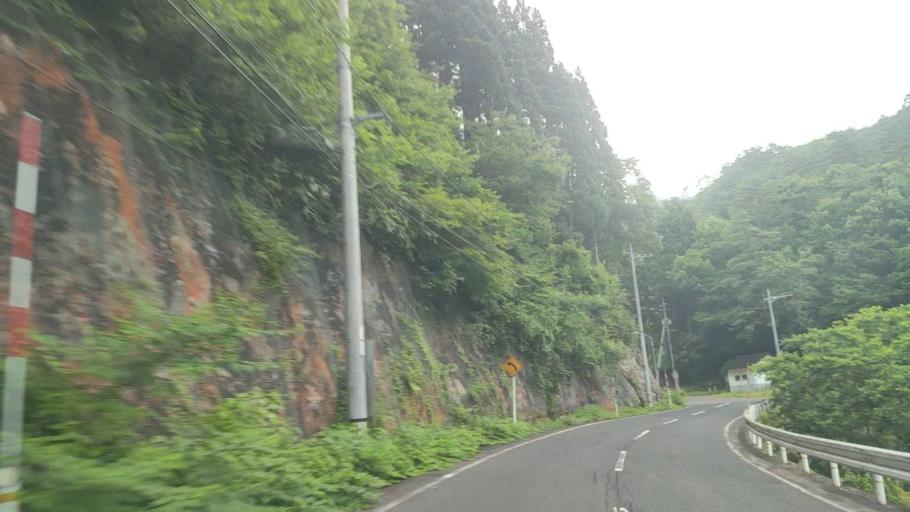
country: JP
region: Tottori
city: Kurayoshi
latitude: 35.3261
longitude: 134.0378
